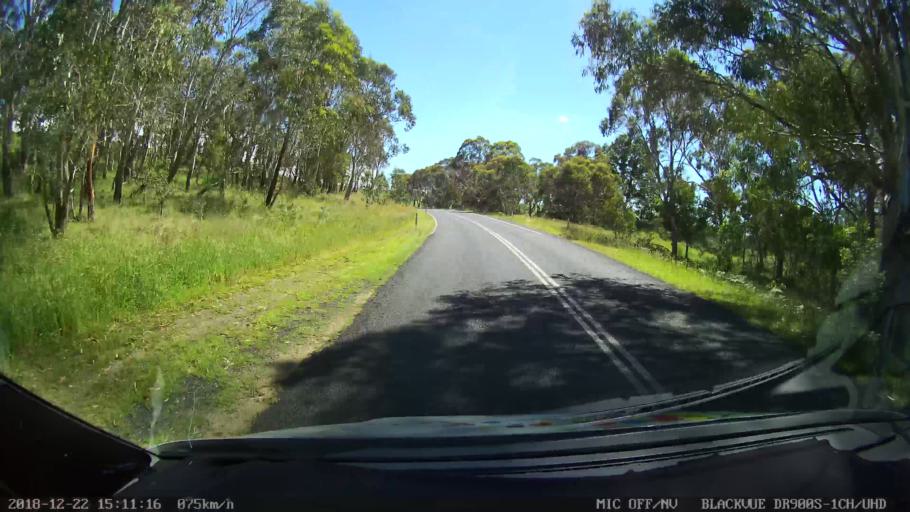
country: AU
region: New South Wales
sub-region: Bellingen
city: Dorrigo
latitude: -30.3427
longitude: 152.4037
